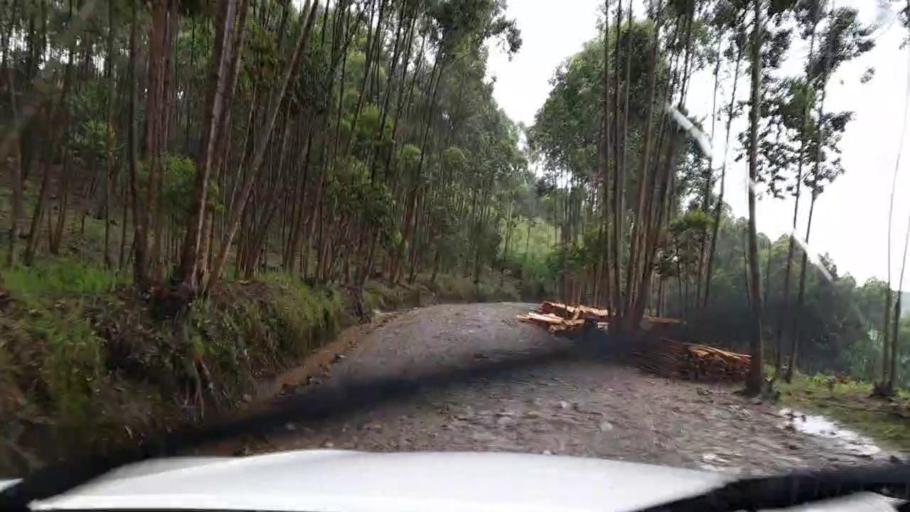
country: RW
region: Western Province
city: Cyangugu
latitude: -2.4680
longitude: 29.0344
